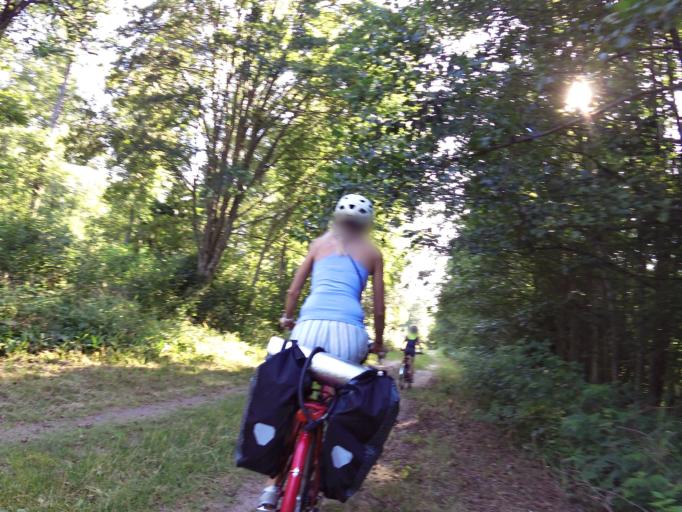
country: EE
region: Hiiumaa
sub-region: Kaerdla linn
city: Kardla
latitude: 58.7765
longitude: 22.4832
